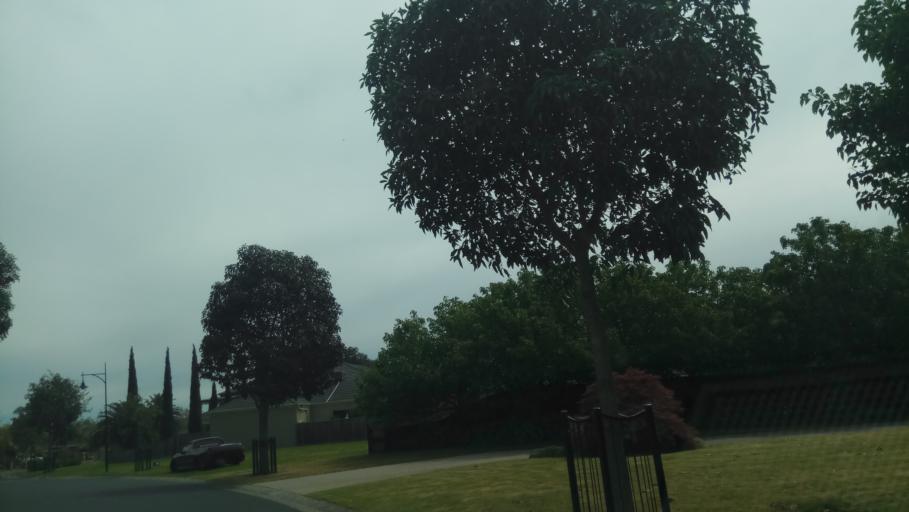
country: AU
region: Victoria
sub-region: Kingston
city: Dingley Village
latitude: -37.9691
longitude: 145.1332
